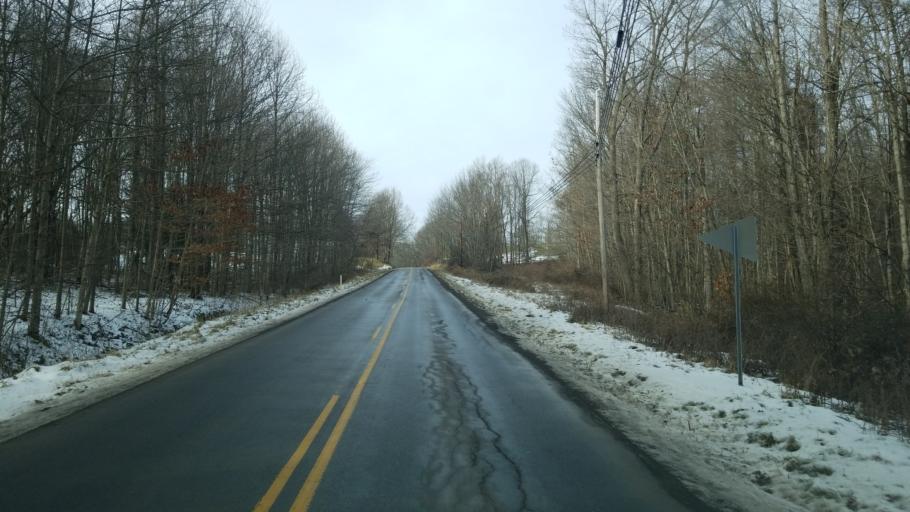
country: US
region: Pennsylvania
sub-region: Indiana County
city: Johnsonburg
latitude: 40.8364
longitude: -78.8495
